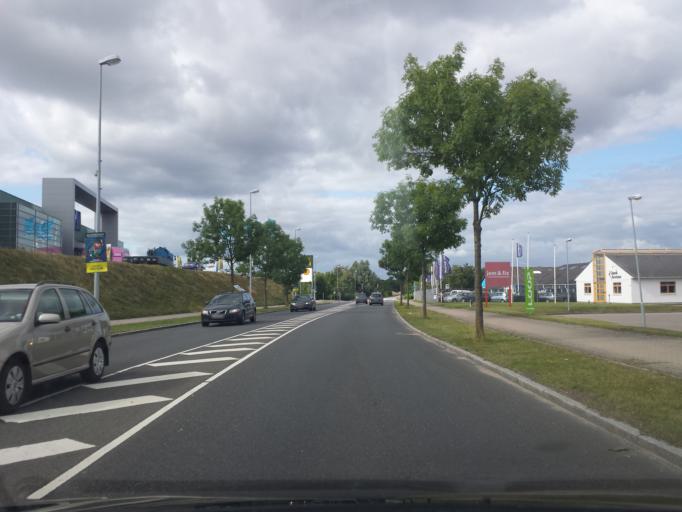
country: DK
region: South Denmark
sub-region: Sonderborg Kommune
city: Sonderborg
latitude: 54.9226
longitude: 9.8085
